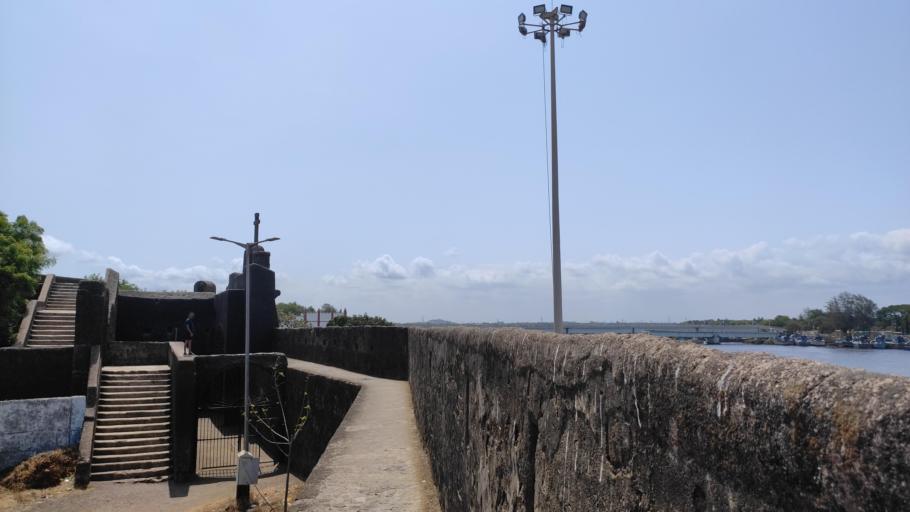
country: IN
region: Daman and Diu
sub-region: Daman District
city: Daman
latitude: 20.4130
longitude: 72.8324
